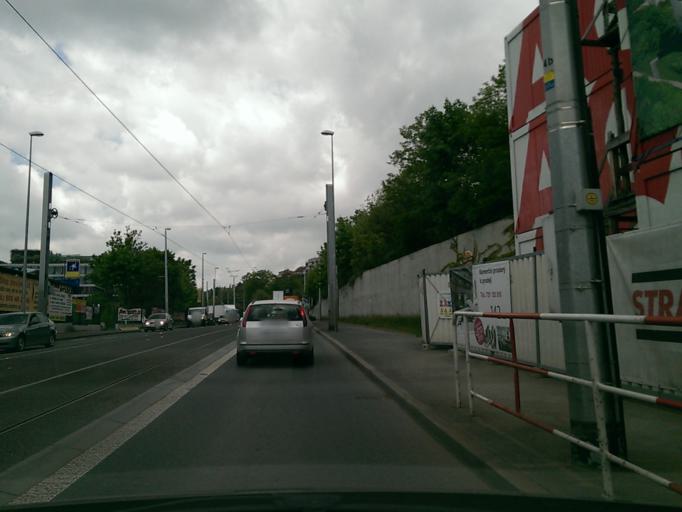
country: CZ
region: Praha
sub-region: Praha 2
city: Vysehrad
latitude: 50.0593
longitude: 14.3920
